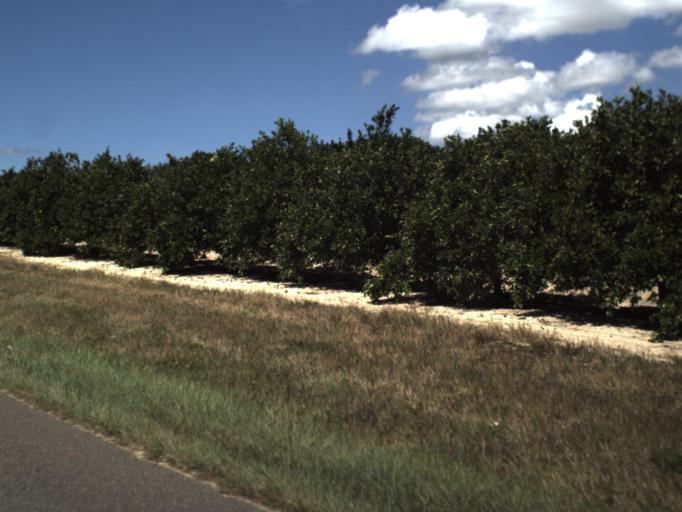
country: US
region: Florida
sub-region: Polk County
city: Babson Park
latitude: 27.8431
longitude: -81.5397
